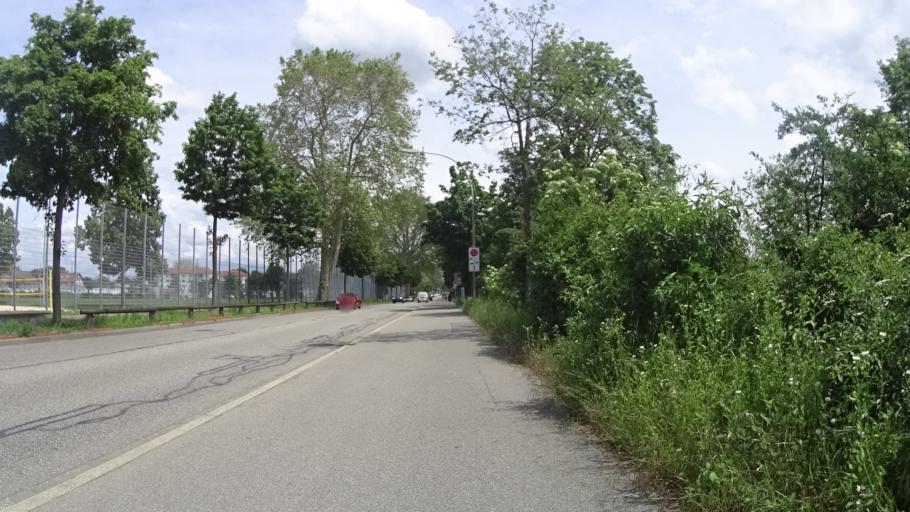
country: CH
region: Basel-Landschaft
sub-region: Bezirk Arlesheim
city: Birsfelden
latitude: 47.5612
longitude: 7.6221
